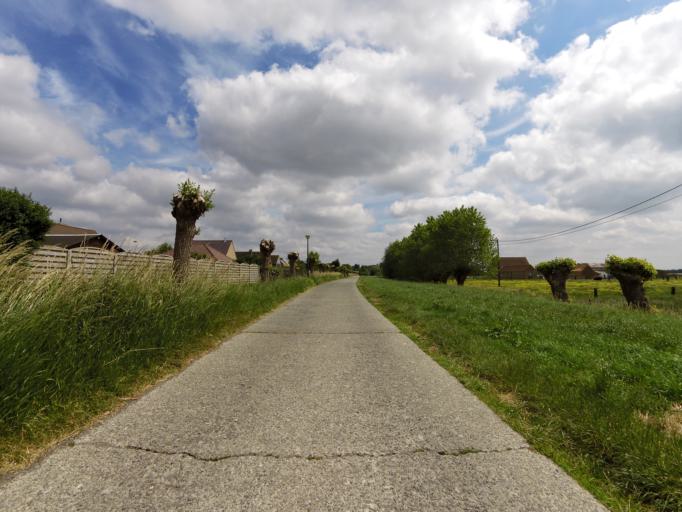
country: BE
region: Flanders
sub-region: Provincie West-Vlaanderen
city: Oudenburg
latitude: 51.1955
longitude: 2.9783
